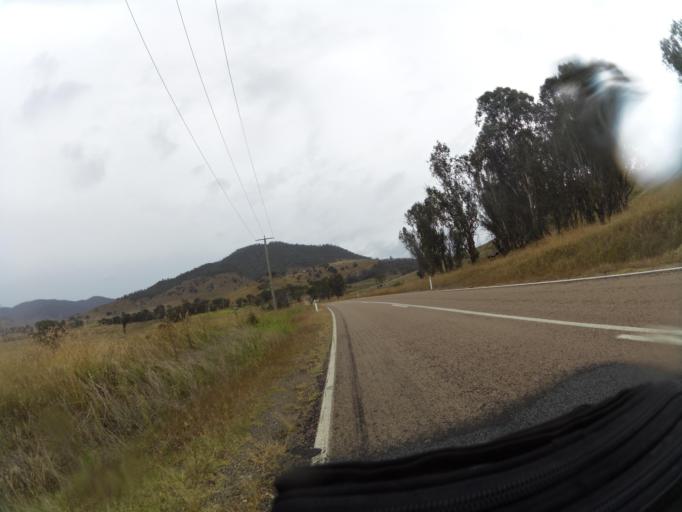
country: AU
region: New South Wales
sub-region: Greater Hume Shire
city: Holbrook
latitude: -36.2152
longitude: 147.7304
